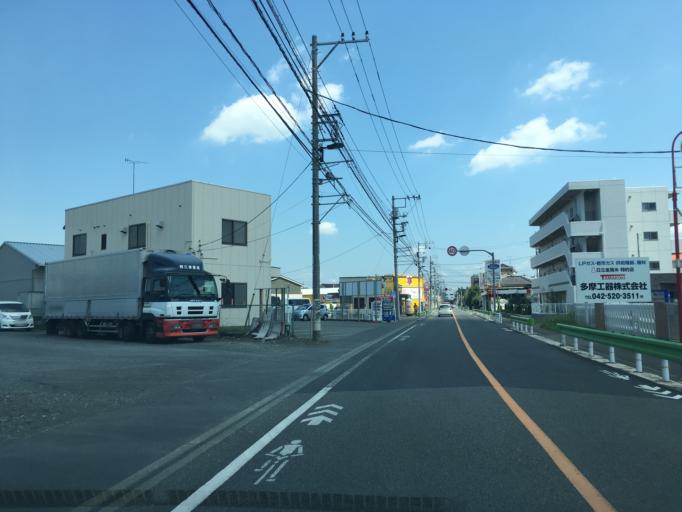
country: JP
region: Tokyo
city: Fussa
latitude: 35.7282
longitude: 139.3568
